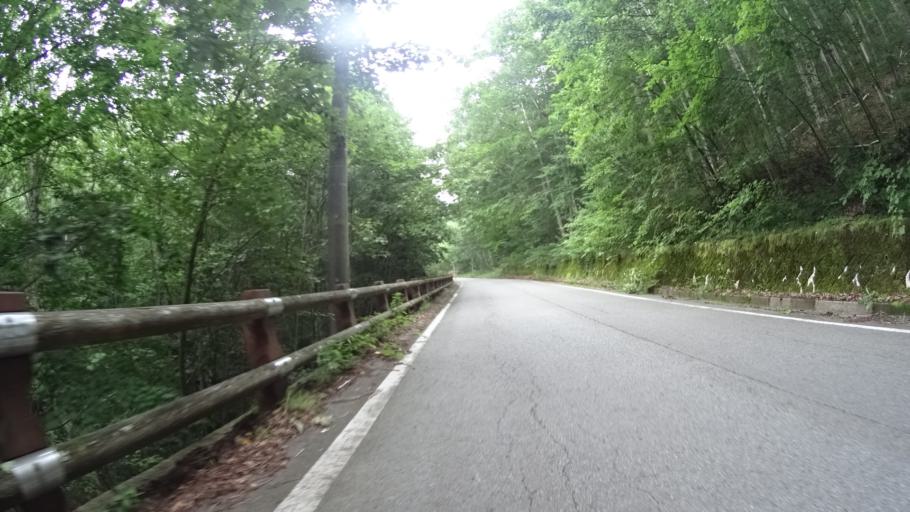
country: JP
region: Yamanashi
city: Nirasaki
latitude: 35.8922
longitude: 138.5612
